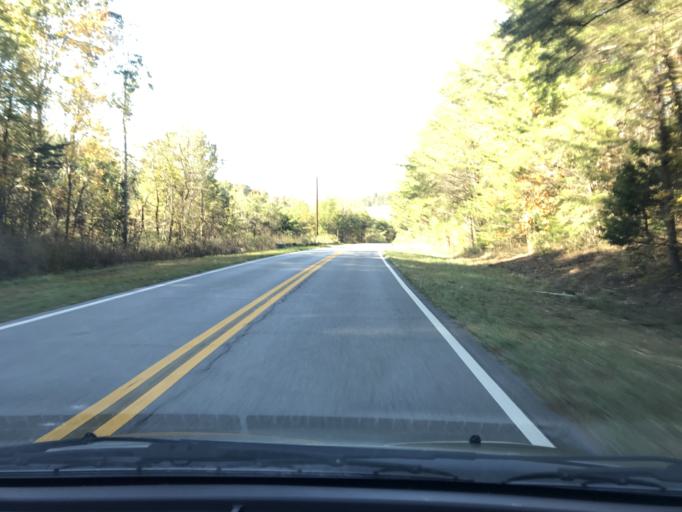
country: US
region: Georgia
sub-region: Dade County
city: Trenton
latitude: 34.8837
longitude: -85.4669
